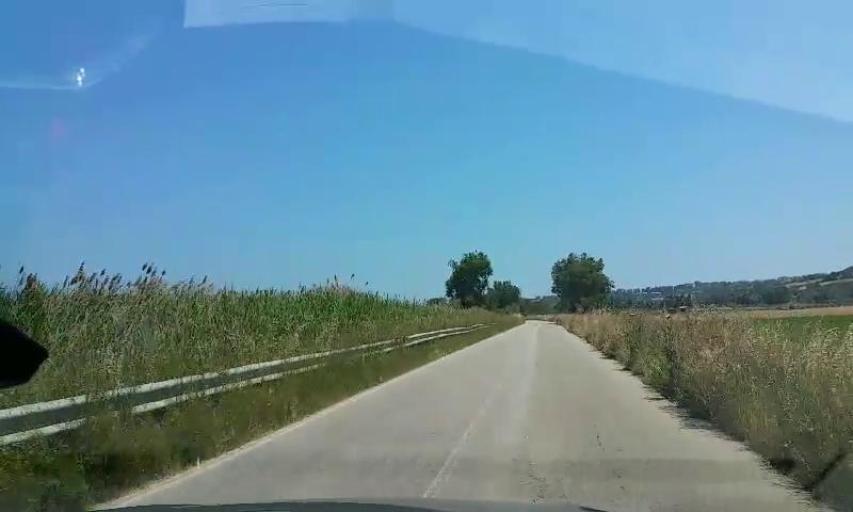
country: IT
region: Molise
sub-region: Provincia di Campobasso
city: San Giacomo degli Schiavoni
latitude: 41.9906
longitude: 14.9438
